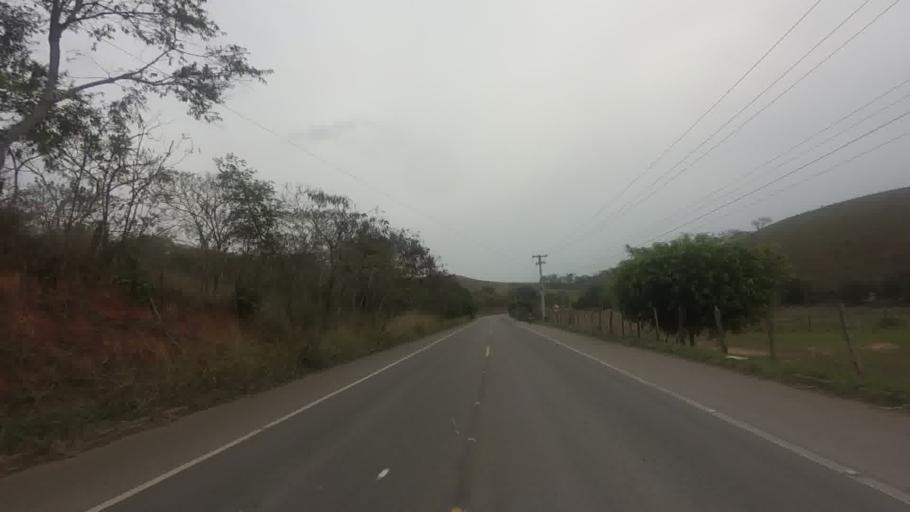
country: BR
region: Rio de Janeiro
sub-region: Santo Antonio De Padua
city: Santo Antonio de Padua
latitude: -21.5739
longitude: -42.2084
